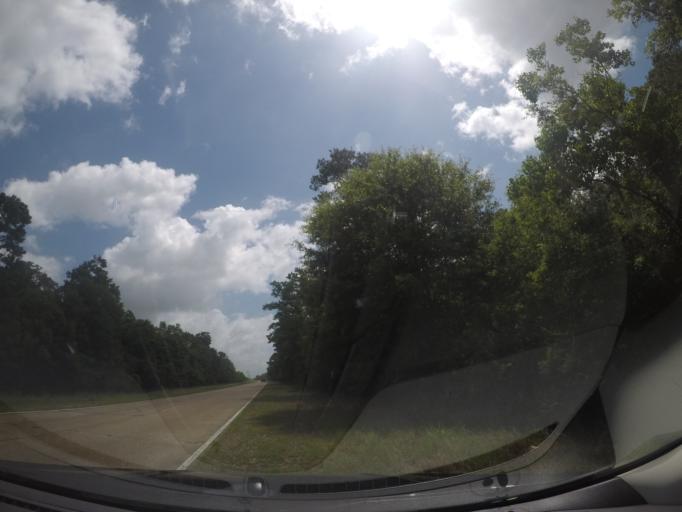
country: US
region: Mississippi
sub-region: Hancock County
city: Pearlington
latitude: 30.2063
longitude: -89.6982
